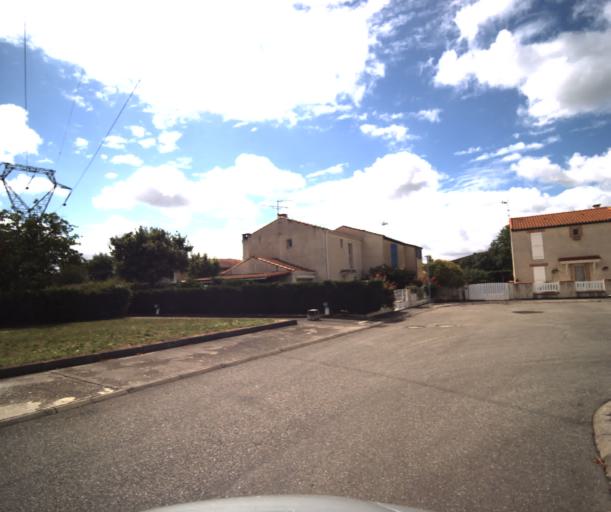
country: FR
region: Midi-Pyrenees
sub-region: Departement de la Haute-Garonne
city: Pinsaguel
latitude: 43.5173
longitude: 1.3937
